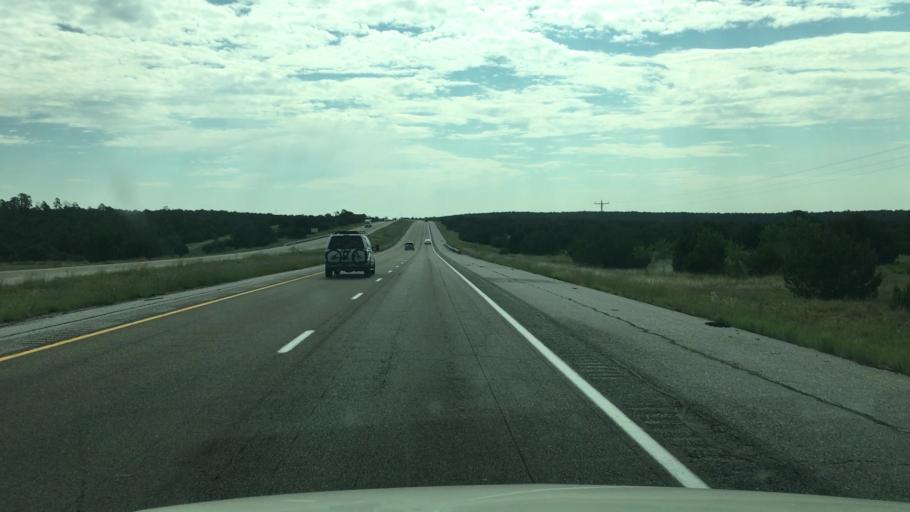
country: US
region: New Mexico
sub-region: Torrance County
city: Moriarty
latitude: 35.0028
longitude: -105.5721
